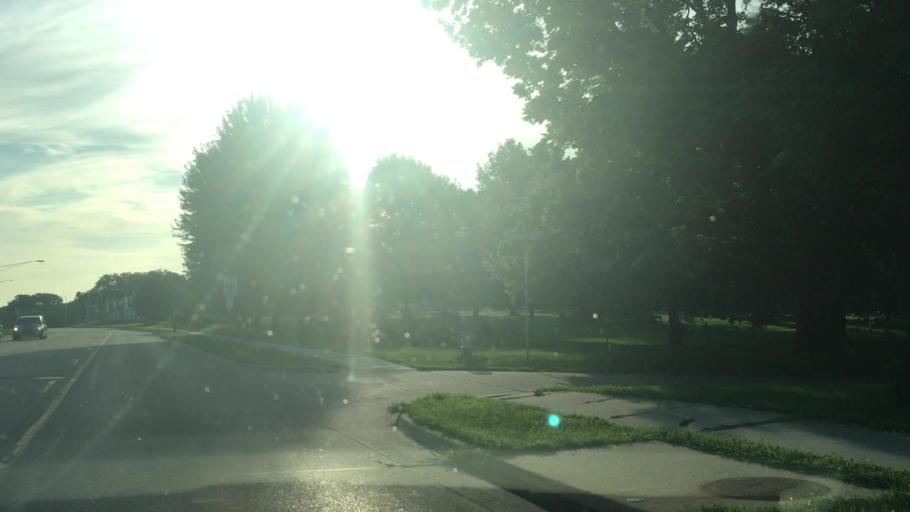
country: US
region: Iowa
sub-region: Johnson County
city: Iowa City
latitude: 41.6761
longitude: -91.5187
